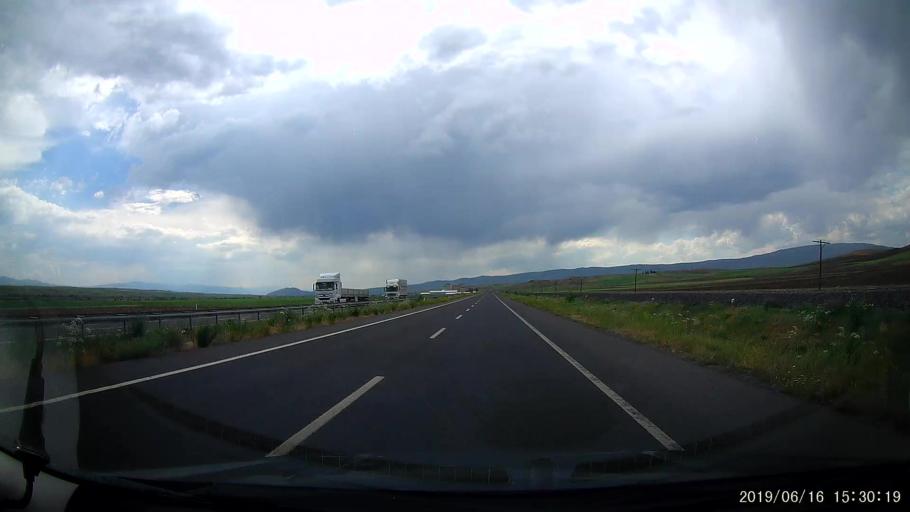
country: TR
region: Erzurum
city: Horasan
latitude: 40.0334
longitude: 42.1091
